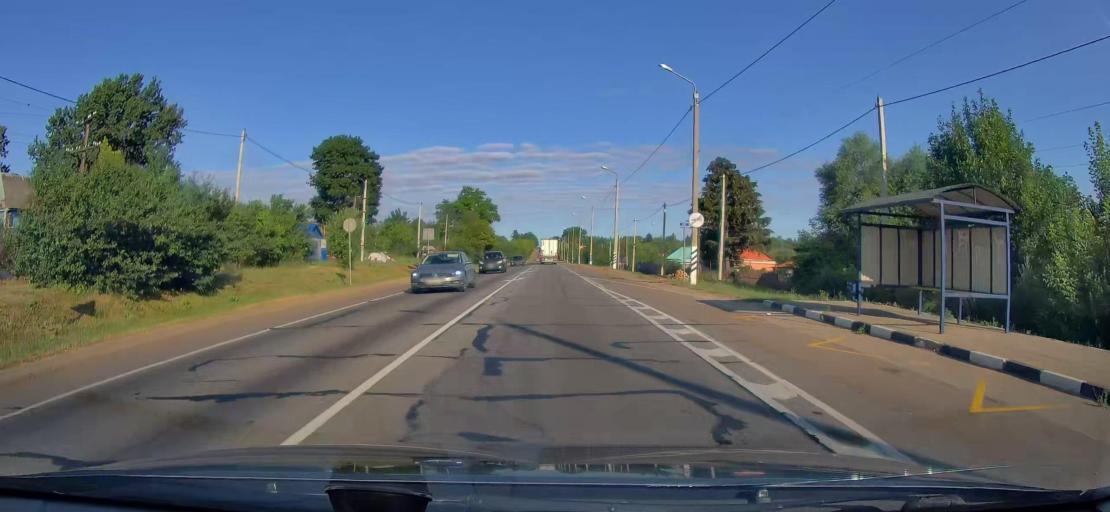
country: RU
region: Tula
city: Chern'
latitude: 53.4513
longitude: 36.8860
